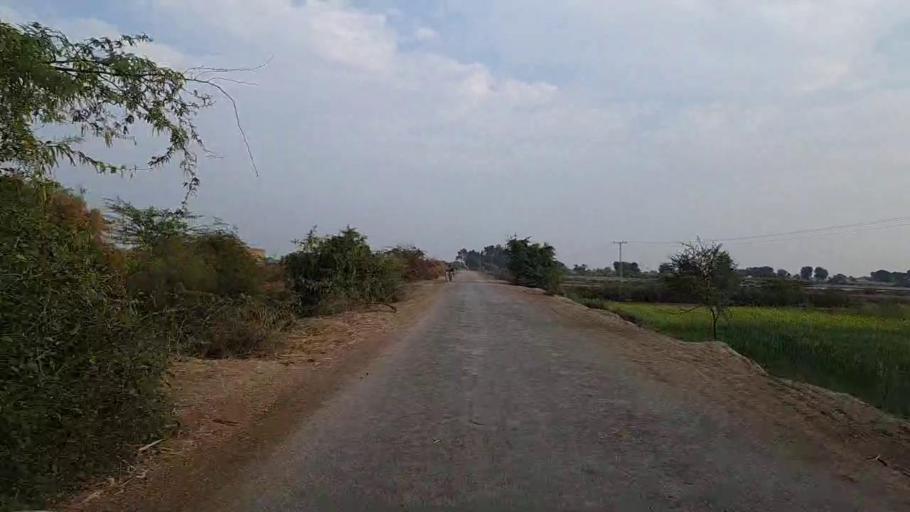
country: PK
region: Sindh
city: Pithoro
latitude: 25.4554
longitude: 69.2811
